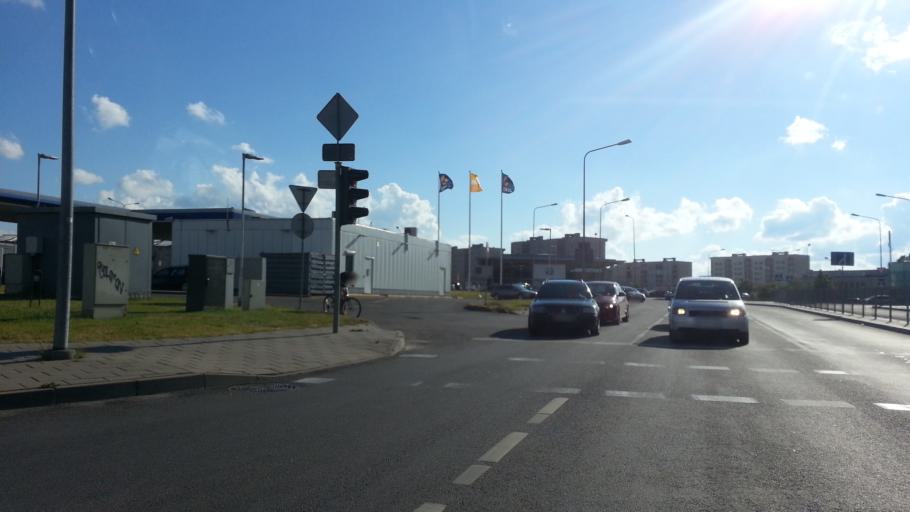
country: LT
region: Vilnius County
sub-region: Vilnius
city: Fabijoniskes
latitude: 54.7309
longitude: 25.2396
